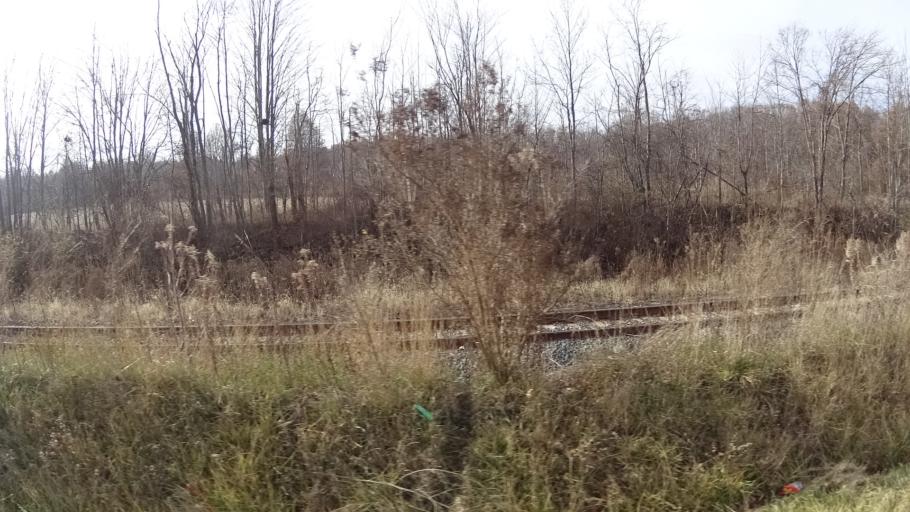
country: US
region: Ohio
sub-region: Lorain County
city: Grafton
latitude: 41.2157
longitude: -81.9947
